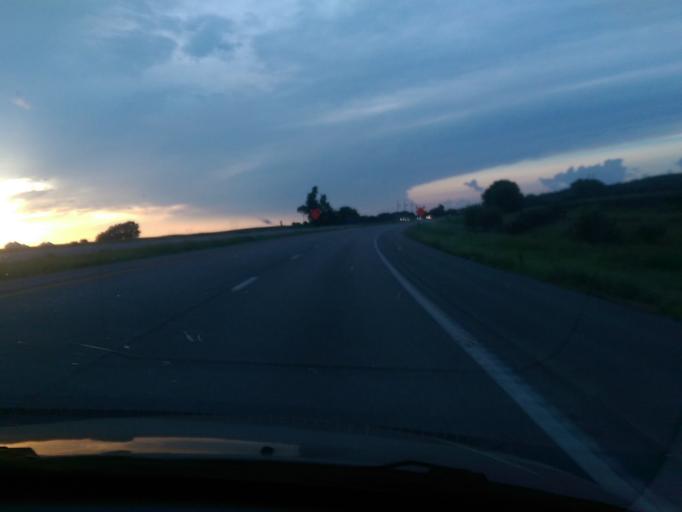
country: US
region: Missouri
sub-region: Atchison County
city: Rock Port
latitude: 40.3492
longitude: -95.5118
